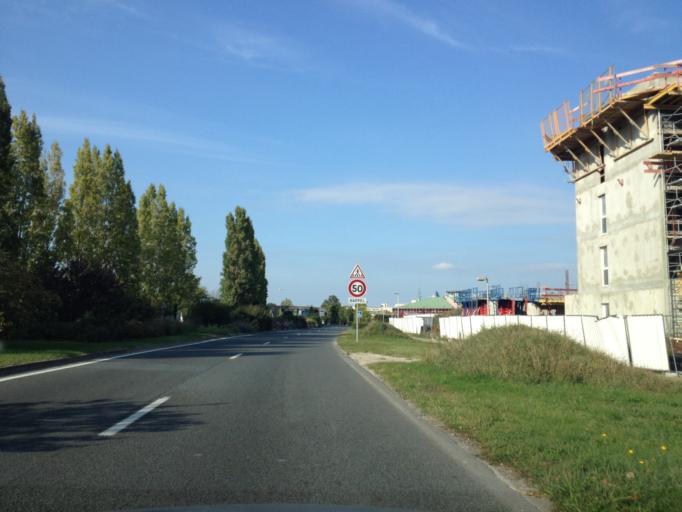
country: FR
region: Rhone-Alpes
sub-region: Departement de l'Isere
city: Villefontaine
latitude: 45.6071
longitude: 5.1563
